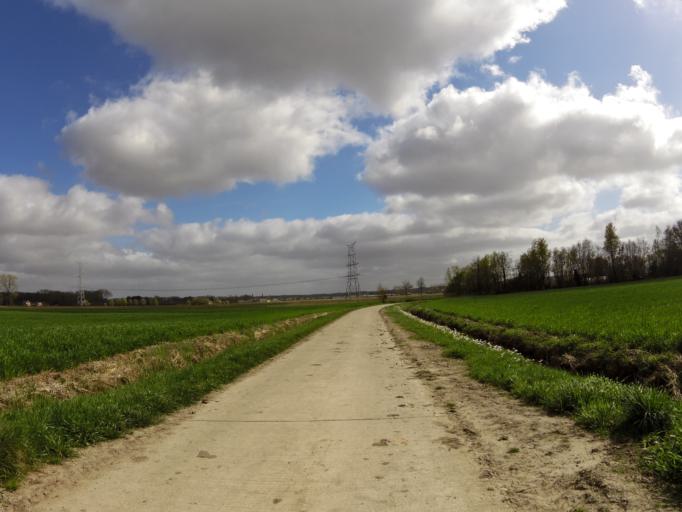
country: BE
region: Flanders
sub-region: Provincie West-Vlaanderen
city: Jabbeke
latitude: 51.2024
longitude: 3.1174
